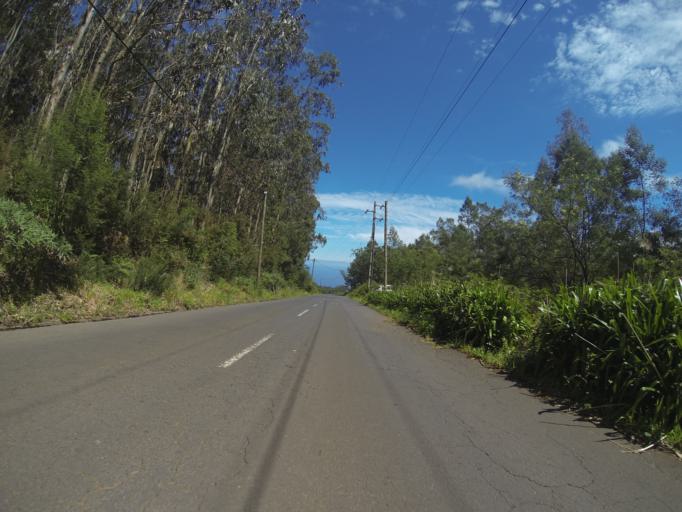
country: PT
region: Madeira
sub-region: Santa Cruz
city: Camacha
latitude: 32.7130
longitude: -16.8304
